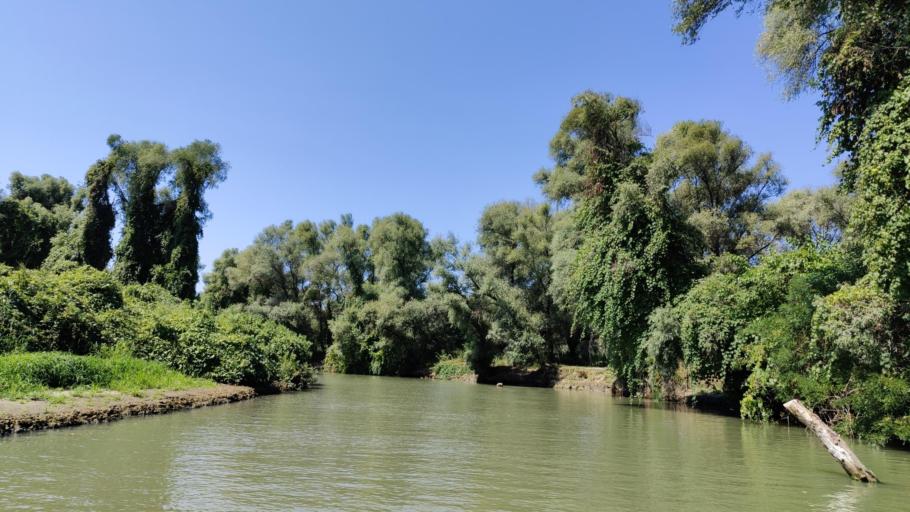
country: RO
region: Tulcea
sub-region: Comuna Pardina
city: Pardina
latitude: 45.2556
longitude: 28.9414
